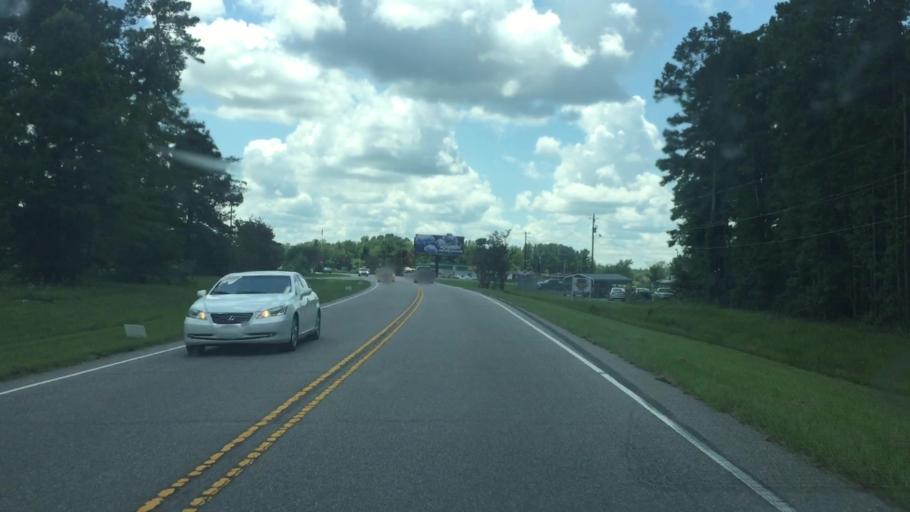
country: US
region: North Carolina
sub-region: Columbus County
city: Tabor City
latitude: 34.1363
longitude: -78.8739
